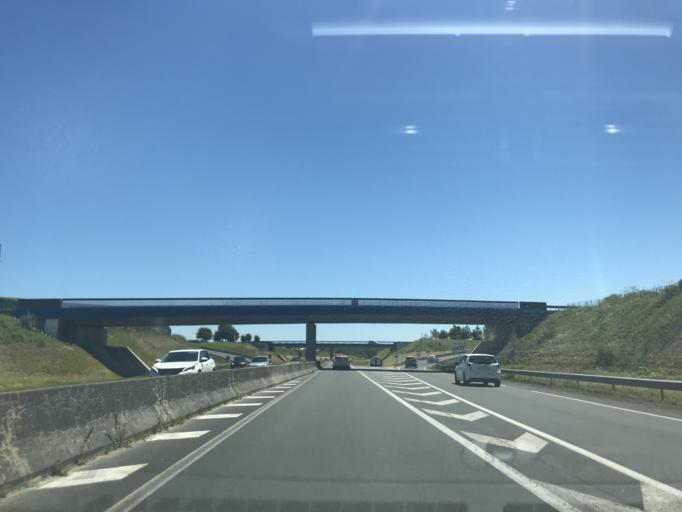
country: FR
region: Poitou-Charentes
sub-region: Departement de la Charente-Maritime
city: Saint-Georges-de-Didonne
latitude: 45.6072
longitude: -0.9751
